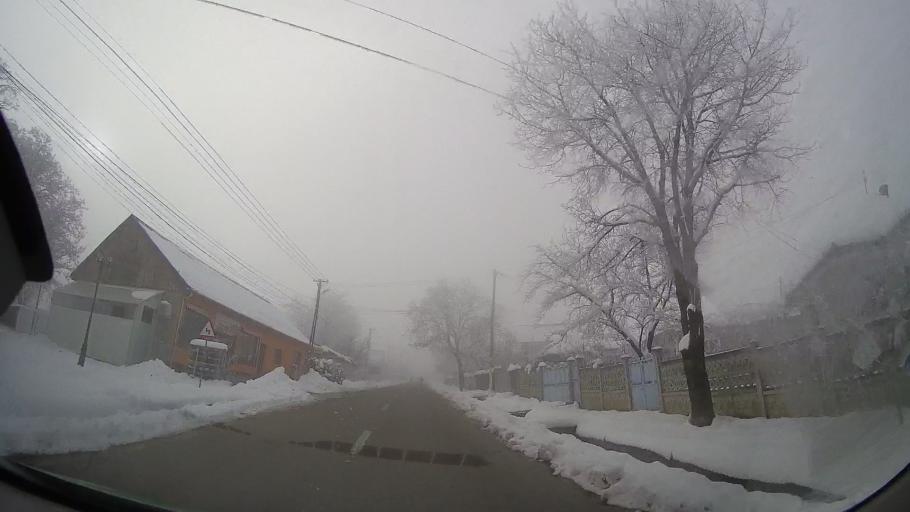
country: RO
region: Iasi
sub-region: Comuna Valea Seaca
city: Topile
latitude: 47.2657
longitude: 26.6699
